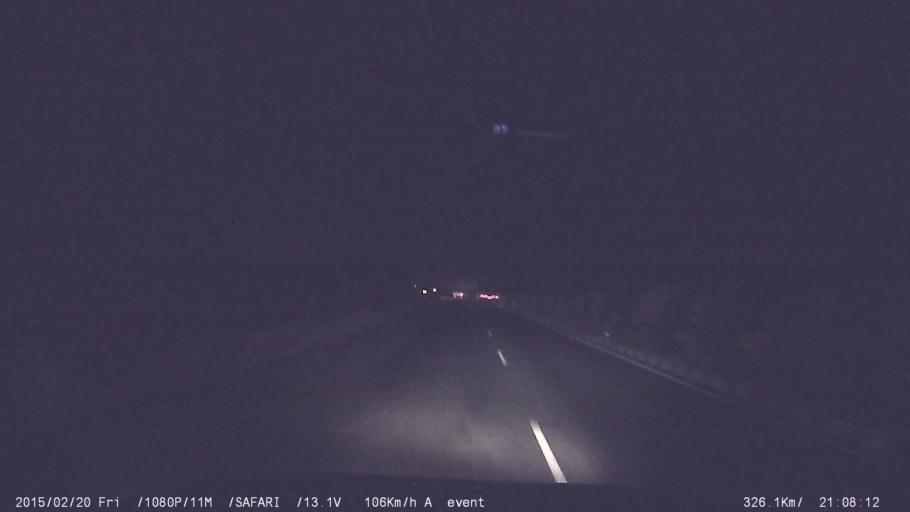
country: IN
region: Tamil Nadu
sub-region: Erode
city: Perundurai
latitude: 11.2726
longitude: 77.5548
